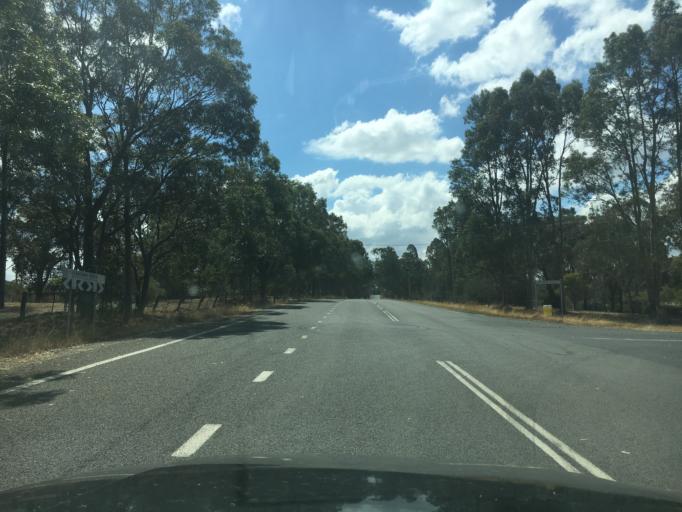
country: AU
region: New South Wales
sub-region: Singleton
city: Singleton
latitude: -32.5166
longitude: 151.1651
